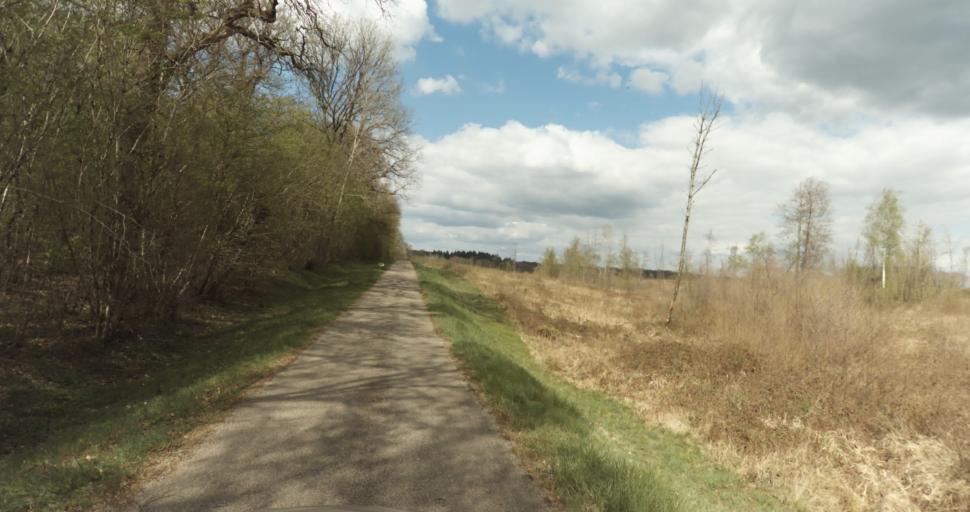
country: FR
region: Bourgogne
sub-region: Departement de la Cote-d'Or
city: Auxonne
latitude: 47.1897
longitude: 5.4519
